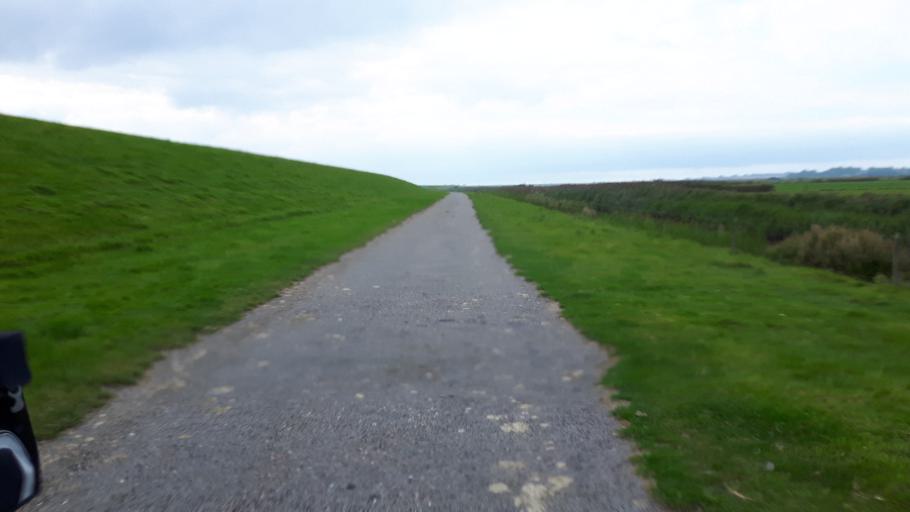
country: NL
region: Friesland
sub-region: Gemeente Ameland
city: Nes
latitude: 53.4421
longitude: 5.8263
